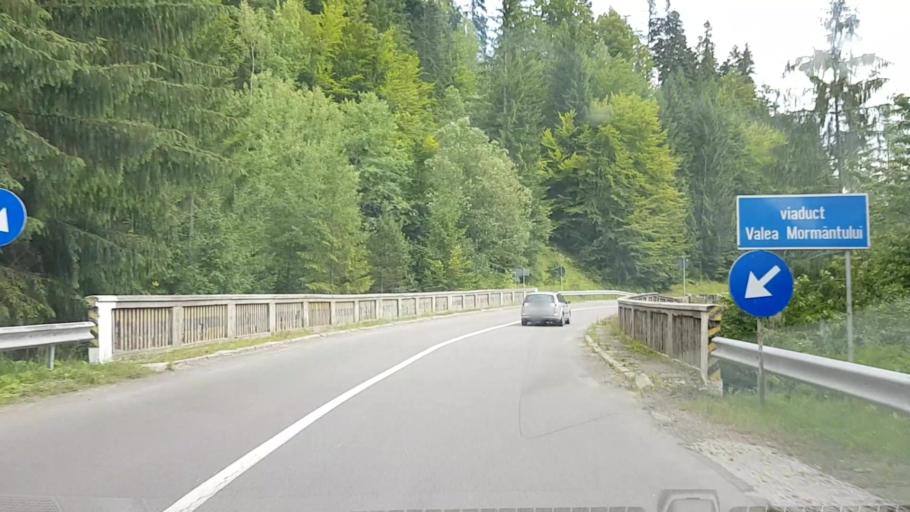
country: RO
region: Neamt
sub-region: Comuna Pangarati
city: Pangarati
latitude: 46.9755
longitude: 26.1169
